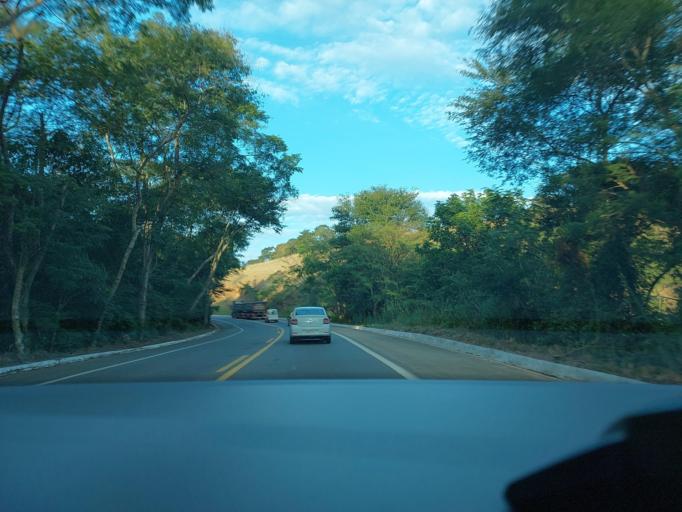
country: BR
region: Minas Gerais
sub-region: Muriae
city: Muriae
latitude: -21.1226
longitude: -42.2171
